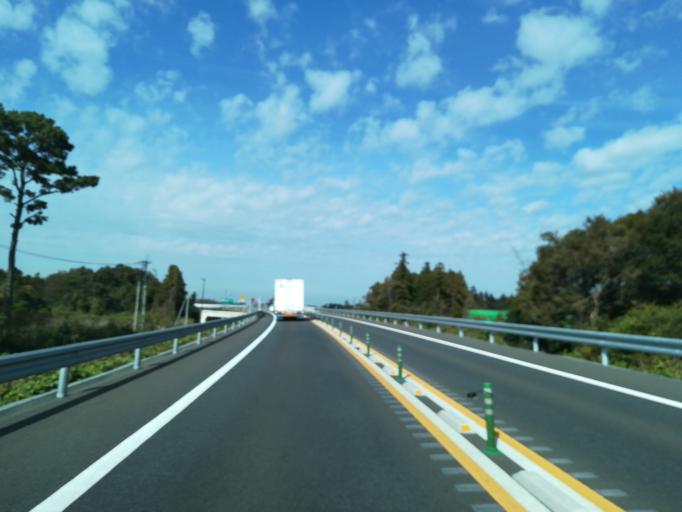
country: JP
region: Ibaraki
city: Ishige
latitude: 36.0757
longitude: 140.0127
